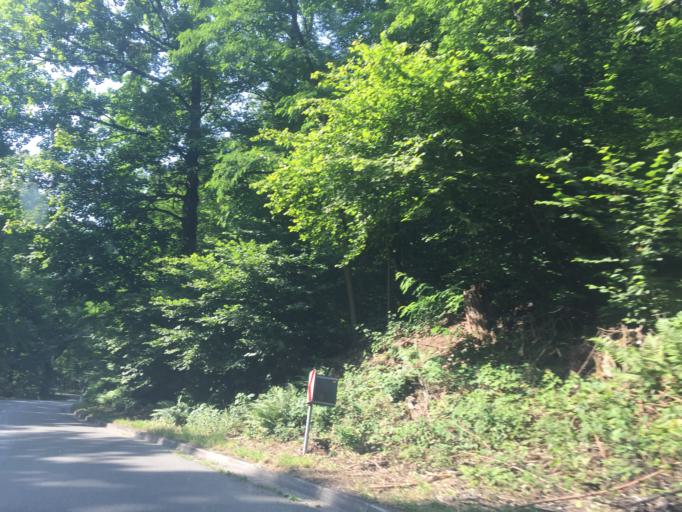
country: DE
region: Baden-Wuerttemberg
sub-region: Karlsruhe Region
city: Heidelberg
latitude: 49.4032
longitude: 8.7197
